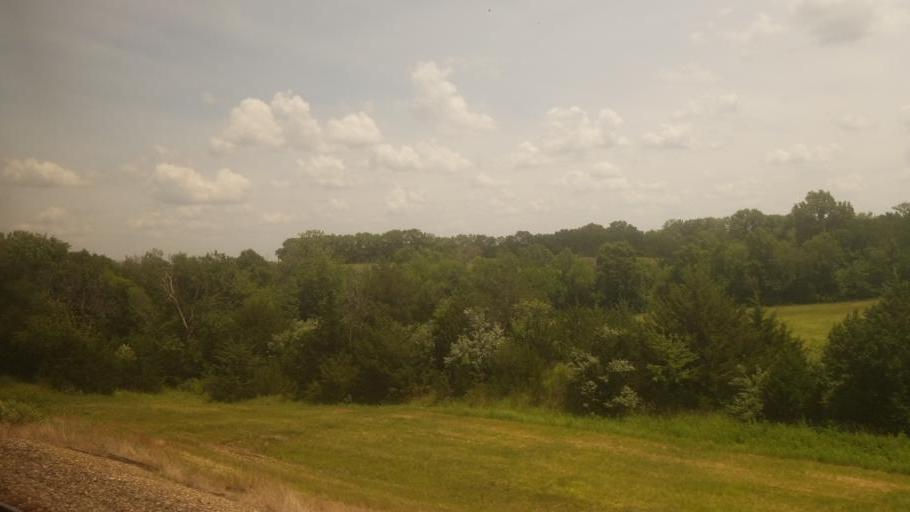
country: US
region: Missouri
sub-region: Macon County
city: La Plata
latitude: 40.0906
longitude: -92.4211
